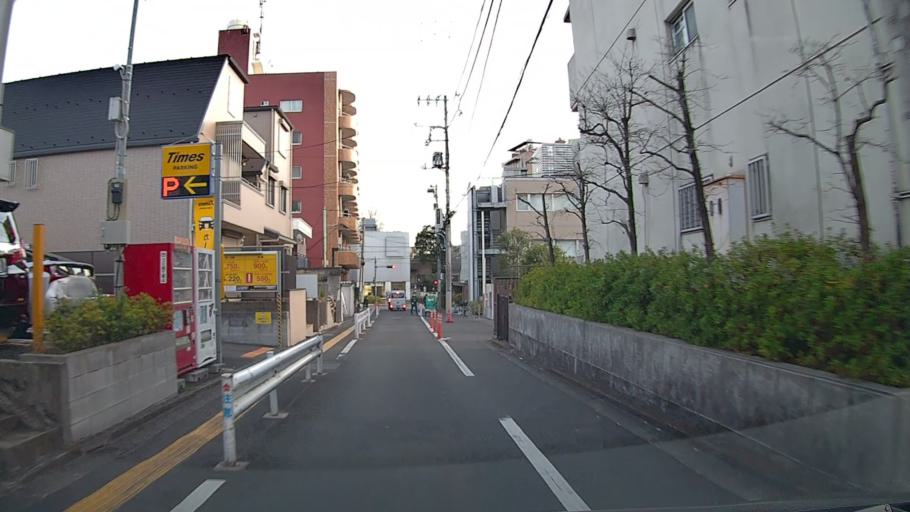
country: JP
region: Tokyo
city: Tokyo
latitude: 35.6999
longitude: 139.7173
